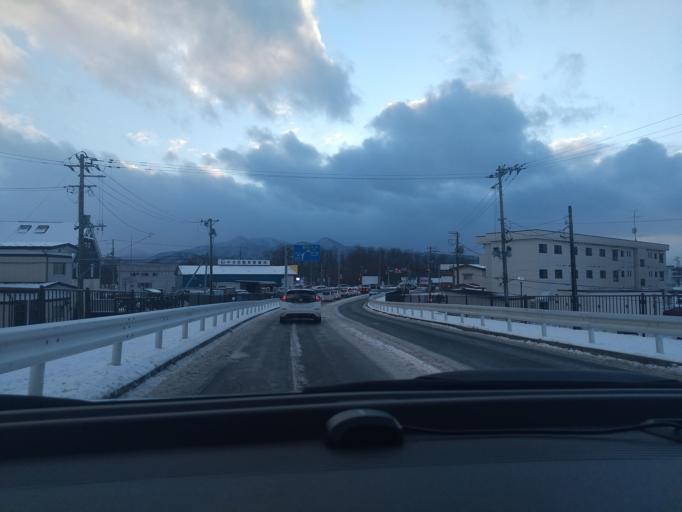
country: JP
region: Iwate
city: Morioka-shi
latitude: 39.7097
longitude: 141.1168
